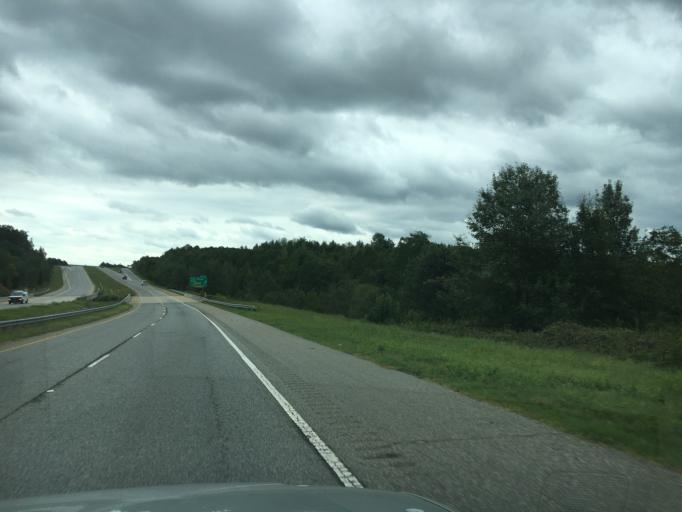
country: US
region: South Carolina
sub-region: Greenville County
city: Mauldin
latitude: 34.7191
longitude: -82.3519
